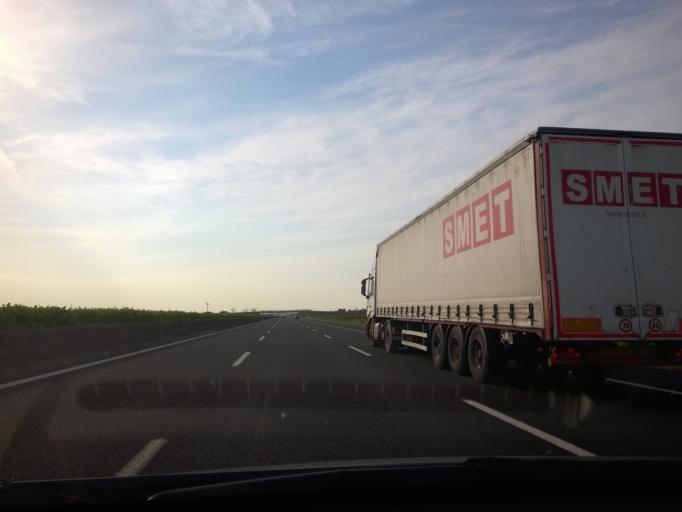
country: IT
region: Emilia-Romagna
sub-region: Forli-Cesena
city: Bagnarola
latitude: 44.1412
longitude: 12.3445
